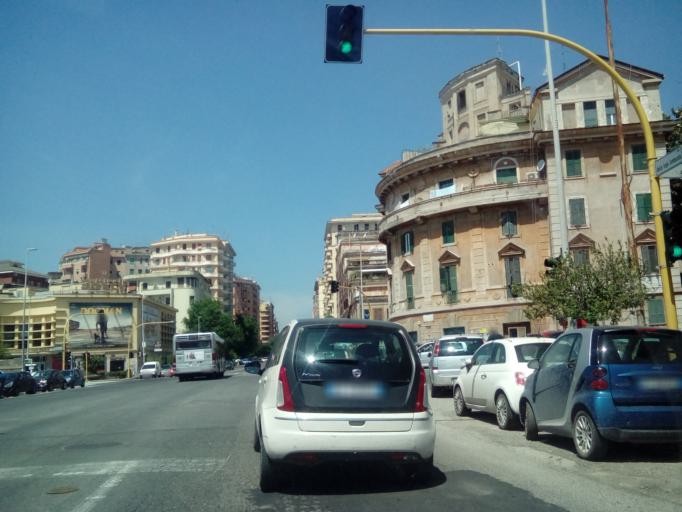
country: IT
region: Latium
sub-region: Citta metropolitana di Roma Capitale
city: Rome
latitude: 41.9087
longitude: 12.5242
